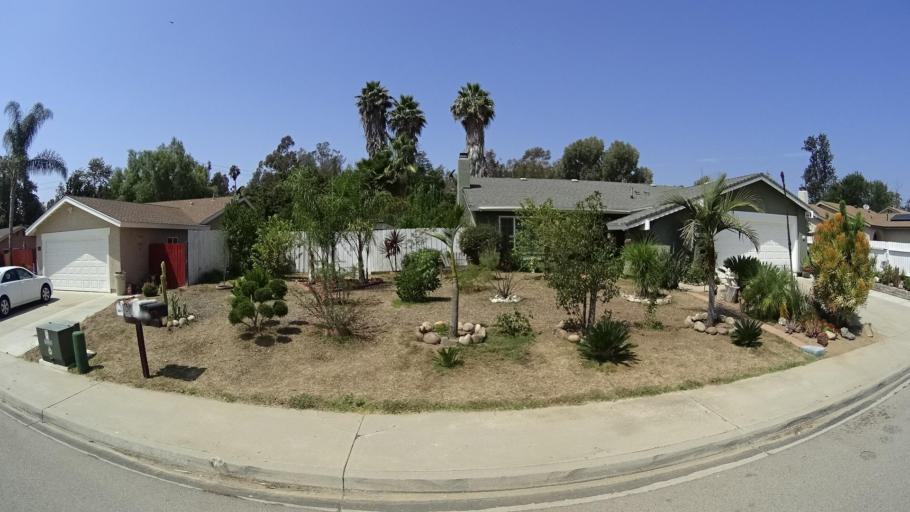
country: US
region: California
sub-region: San Diego County
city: Fallbrook
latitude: 33.3443
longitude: -117.2402
